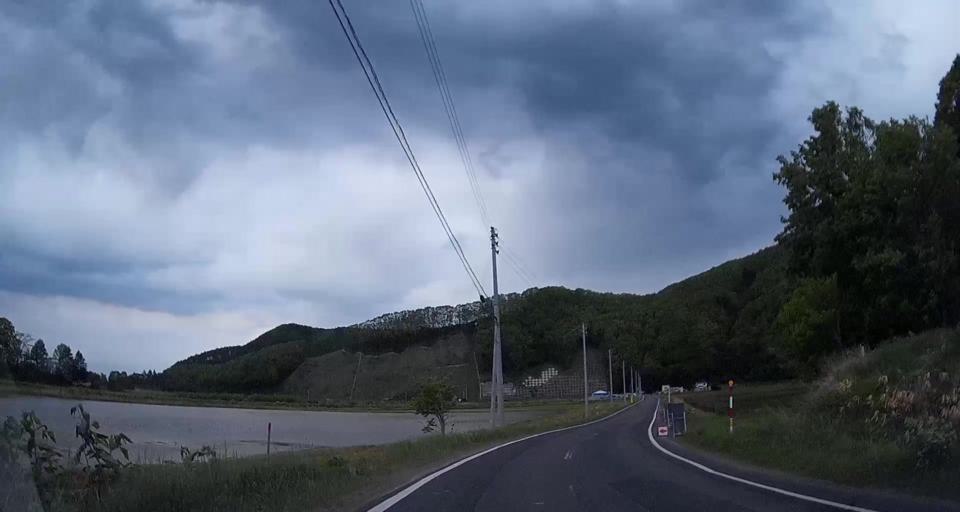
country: JP
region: Hokkaido
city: Chitose
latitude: 42.7584
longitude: 141.9547
